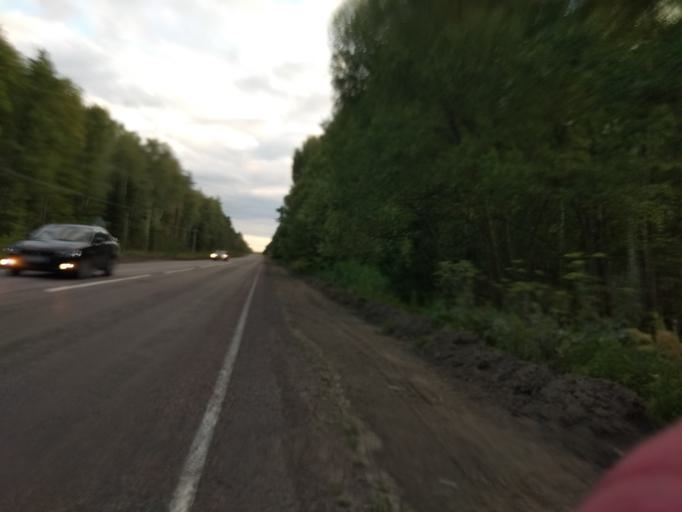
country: RU
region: Moskovskaya
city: Misheronskiy
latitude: 55.6418
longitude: 39.7544
